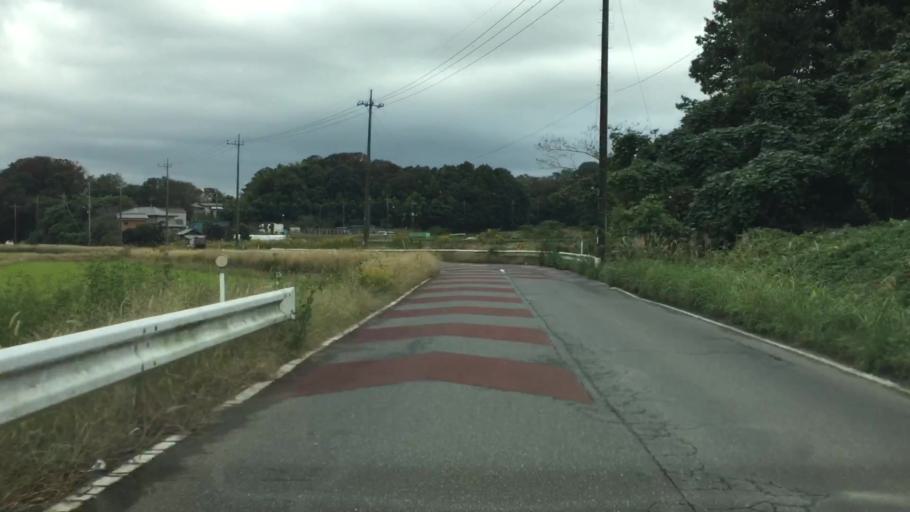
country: JP
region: Chiba
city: Shiroi
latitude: 35.8436
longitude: 140.0890
